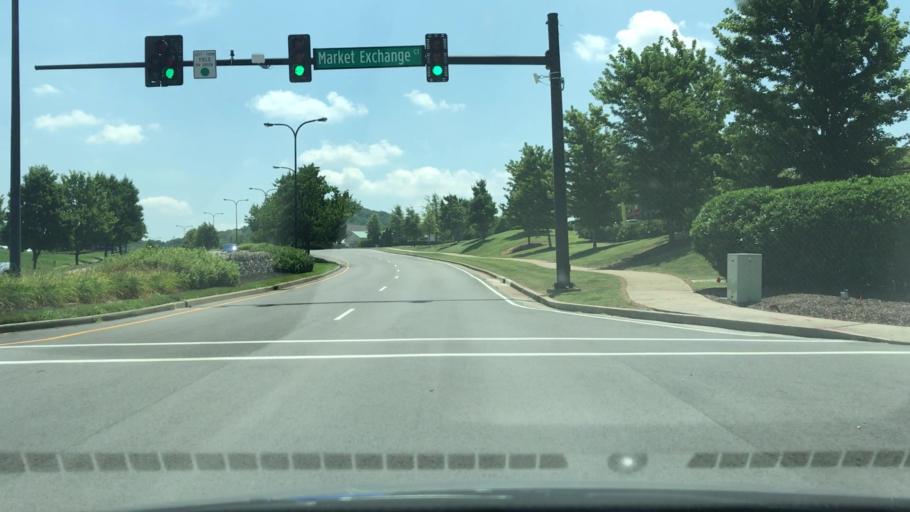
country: US
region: Tennessee
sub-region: Williamson County
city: Brentwood Estates
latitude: 35.9594
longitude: -86.8064
